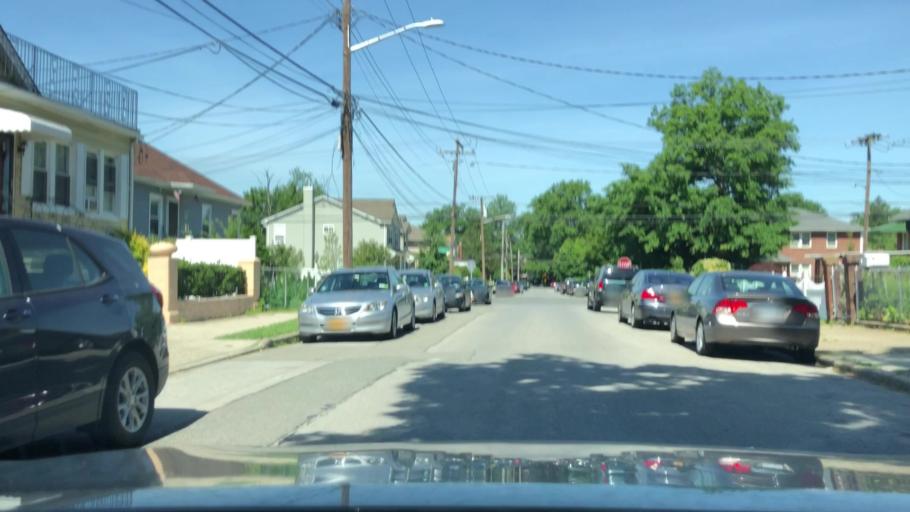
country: US
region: New York
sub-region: Nassau County
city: South Floral Park
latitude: 40.7015
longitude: -73.6964
